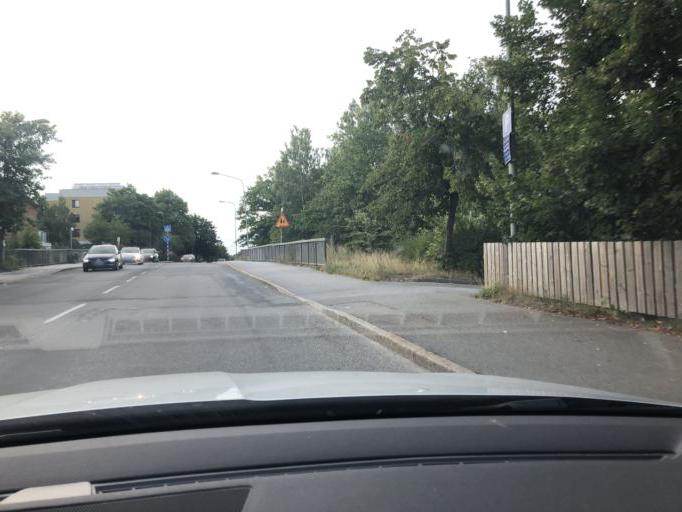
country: SE
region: Stockholm
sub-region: Botkyrka Kommun
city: Fittja
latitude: 59.2734
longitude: 17.8869
